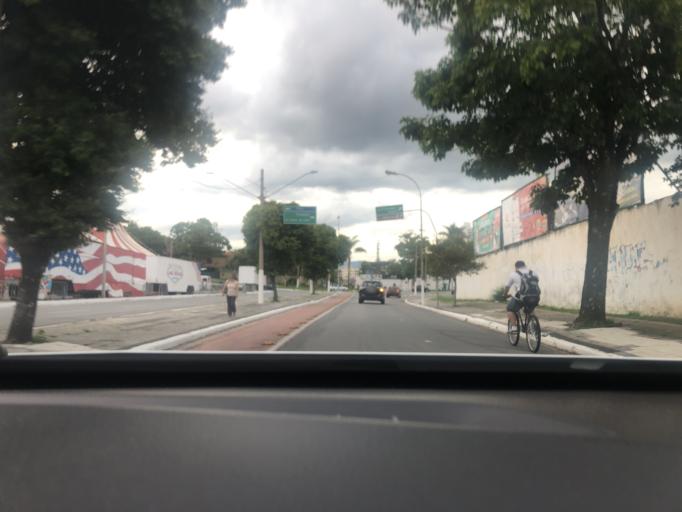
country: BR
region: Sao Paulo
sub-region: Taubate
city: Taubate
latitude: -23.0303
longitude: -45.5697
